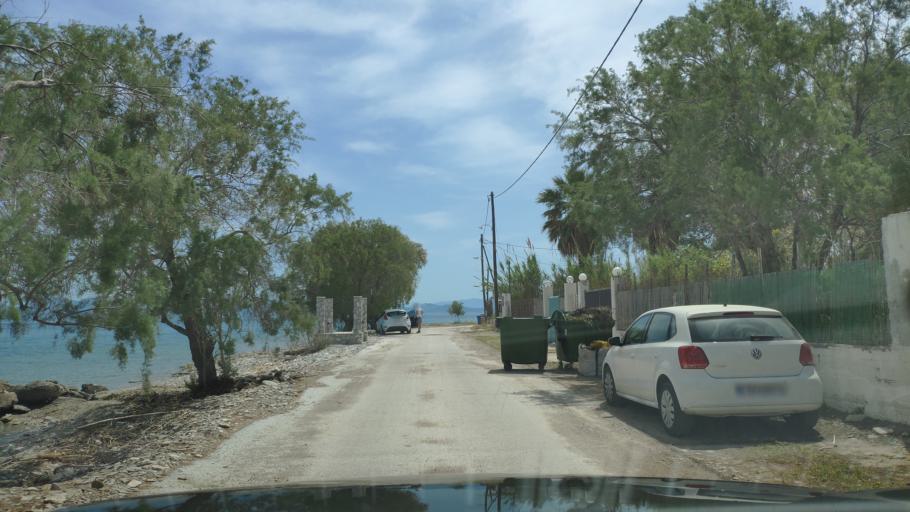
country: GR
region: Attica
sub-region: Nomarchia Anatolikis Attikis
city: Grammatiko
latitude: 38.2623
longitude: 23.9808
